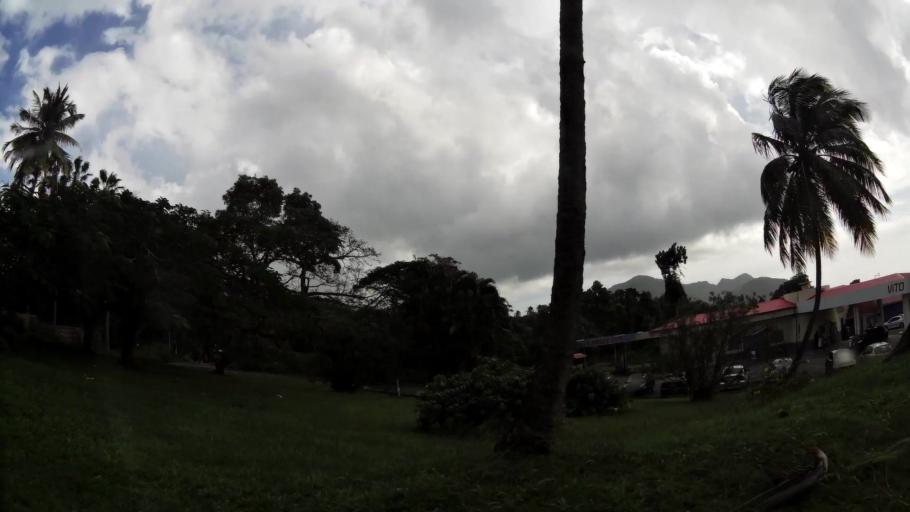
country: GP
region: Guadeloupe
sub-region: Guadeloupe
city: Saint-Claude
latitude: 16.0096
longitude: -61.7098
